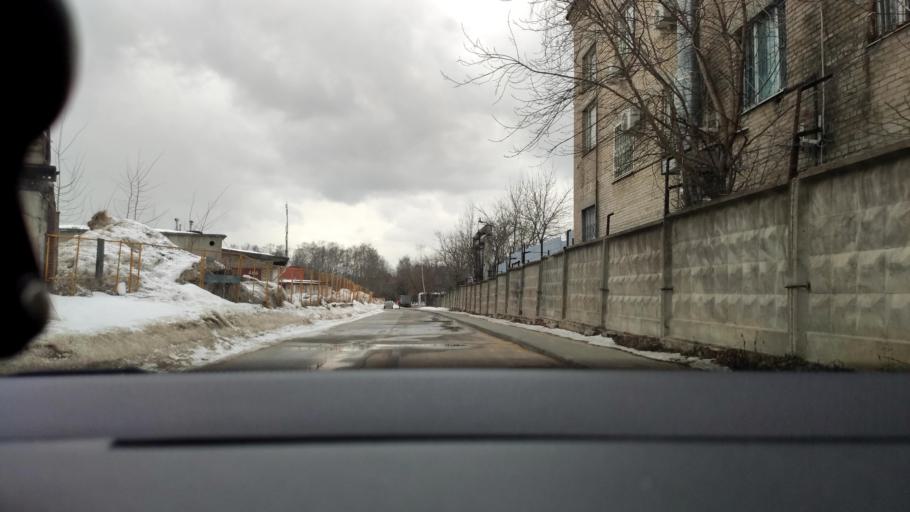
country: RU
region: Moskovskaya
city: Druzhba
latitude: 55.8875
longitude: 37.7595
